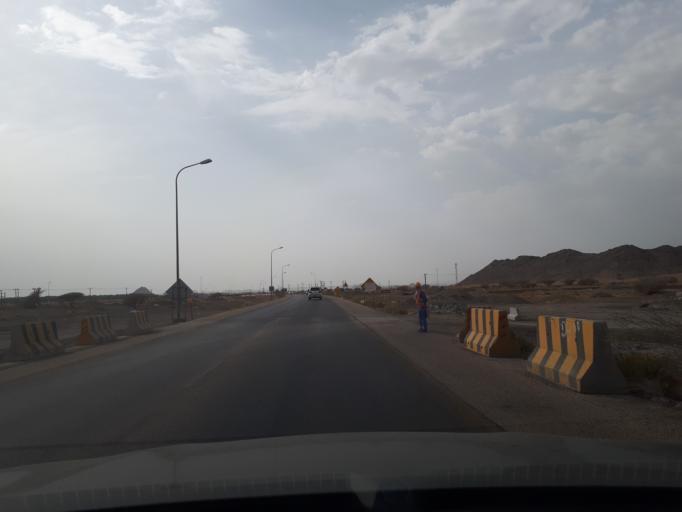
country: OM
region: Ash Sharqiyah
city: Al Qabil
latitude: 22.5598
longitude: 58.7109
